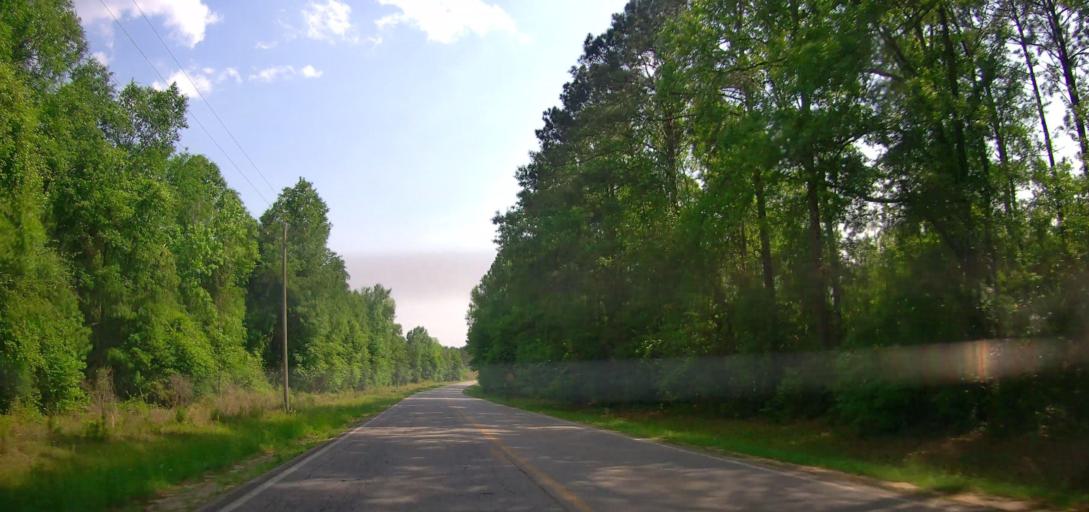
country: US
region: Georgia
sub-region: Laurens County
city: East Dublin
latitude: 32.5825
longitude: -82.8642
